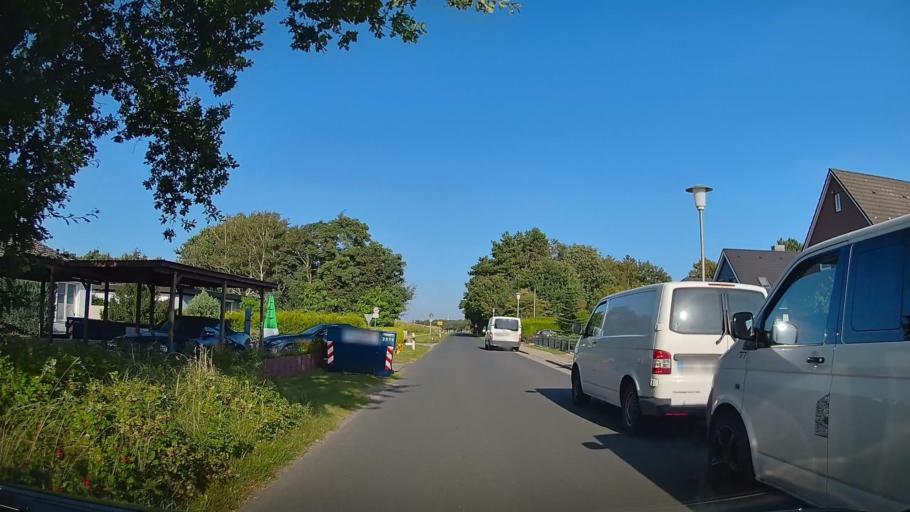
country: DE
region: Lower Saxony
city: Nordholz
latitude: 53.8240
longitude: 8.5913
